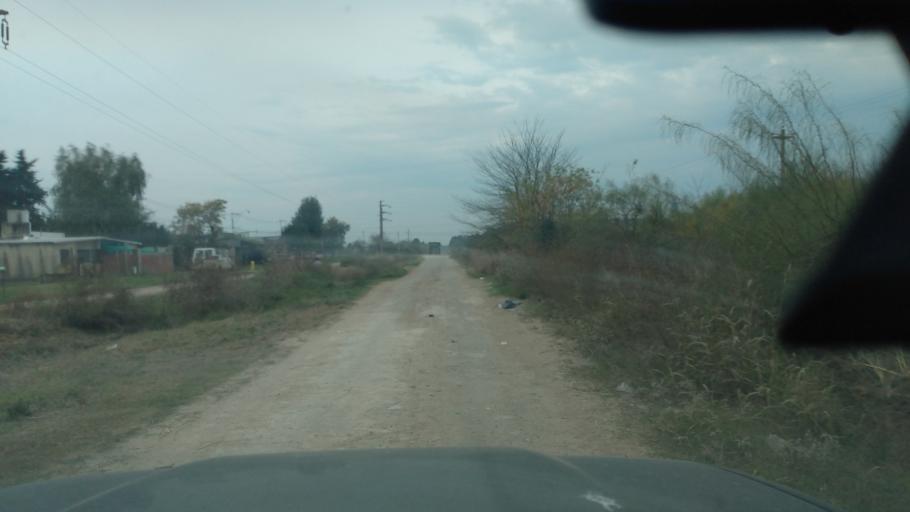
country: AR
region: Buenos Aires
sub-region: Partido de Lujan
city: Lujan
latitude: -34.5629
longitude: -59.1428
